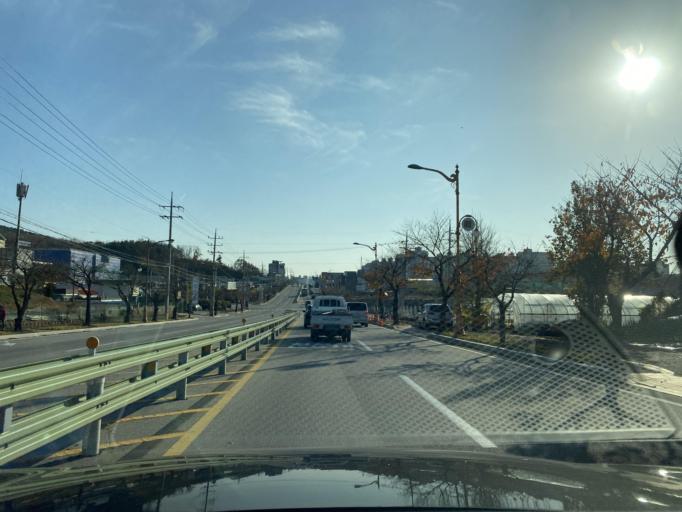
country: KR
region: Chungcheongnam-do
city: Yesan
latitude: 36.7019
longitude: 126.8384
